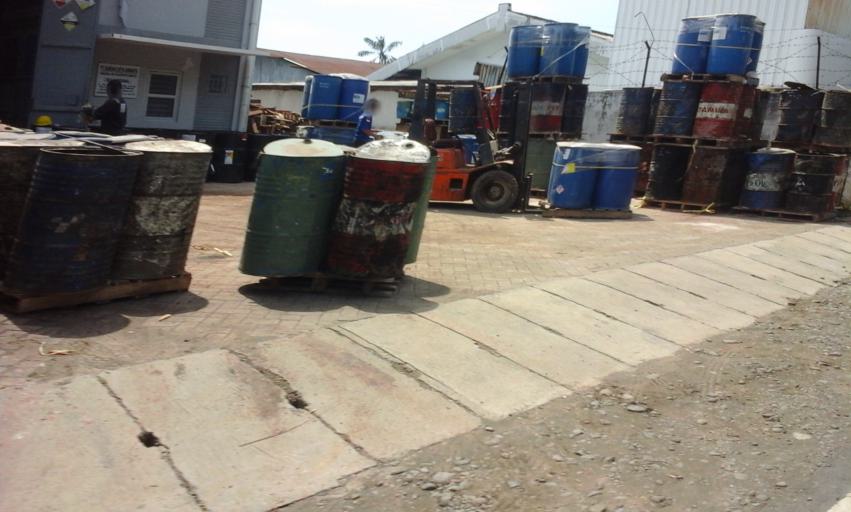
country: ID
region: East Java
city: Kebunjeruk
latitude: -8.1881
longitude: 114.3793
